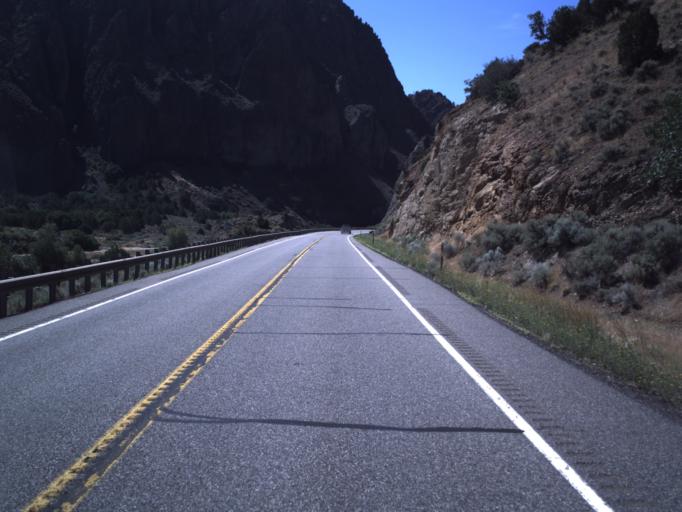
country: US
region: Utah
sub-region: Sevier County
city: Monroe
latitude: 38.5519
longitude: -112.2698
